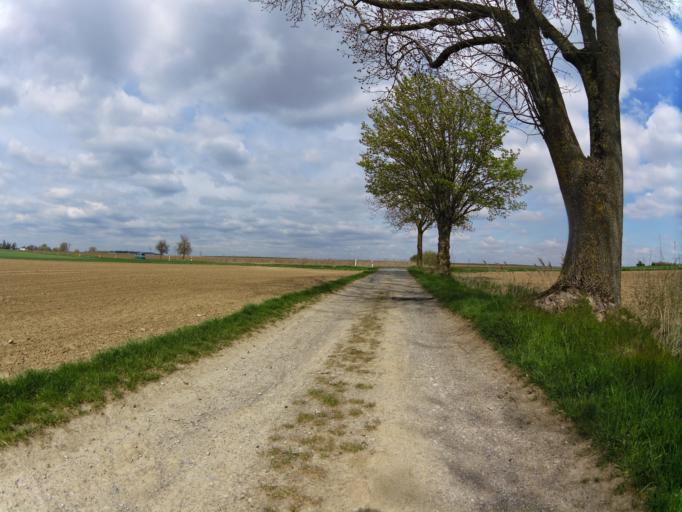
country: DE
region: Bavaria
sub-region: Regierungsbezirk Unterfranken
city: Giebelstadt
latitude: 49.6583
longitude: 9.9374
